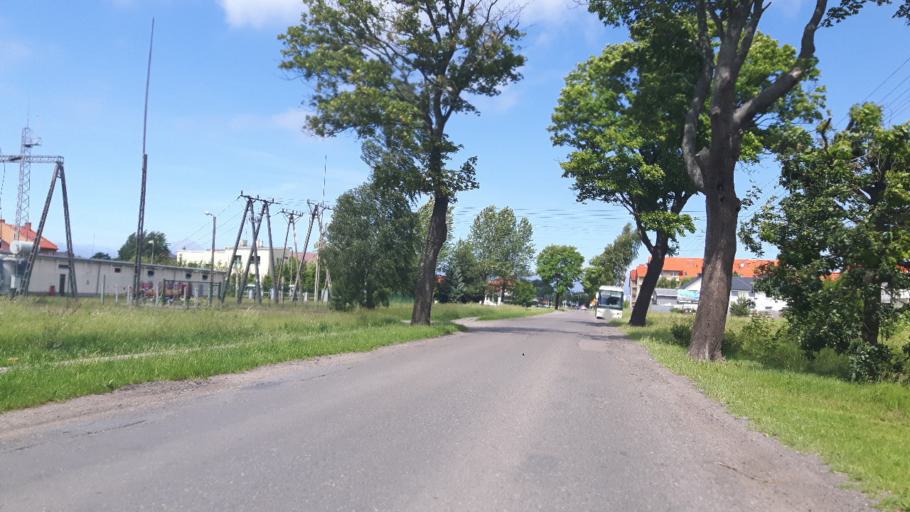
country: PL
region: Pomeranian Voivodeship
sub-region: Powiat slupski
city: Ustka
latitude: 54.5708
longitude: 16.8510
